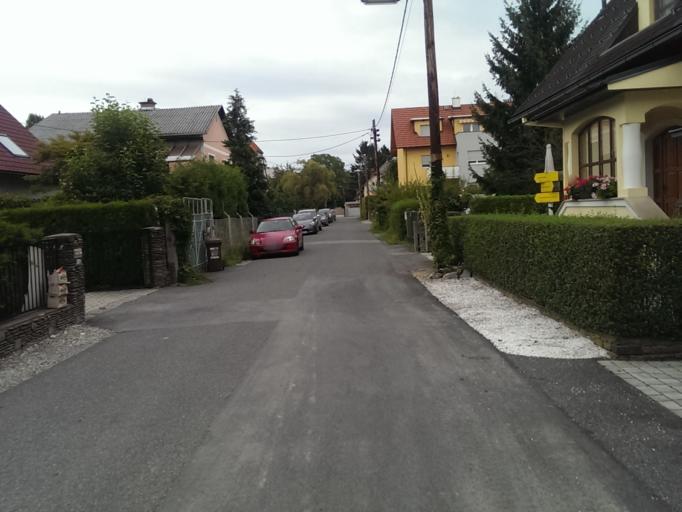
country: AT
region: Styria
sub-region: Graz Stadt
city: Graz
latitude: 47.0545
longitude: 15.4600
